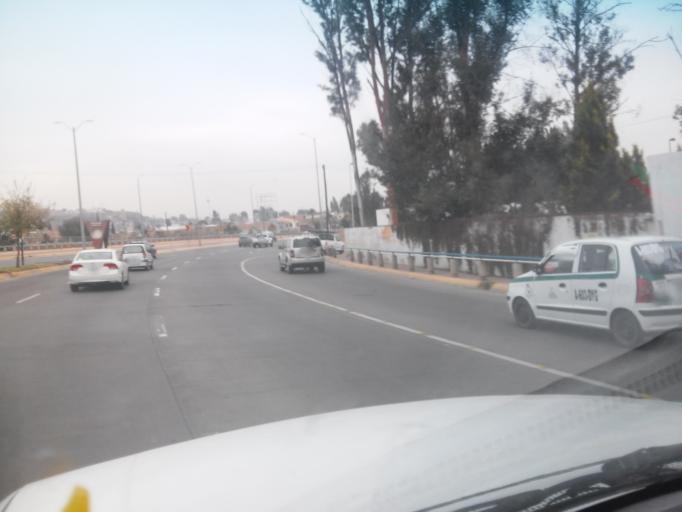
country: MX
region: Durango
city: Victoria de Durango
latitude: 24.0262
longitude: -104.6905
